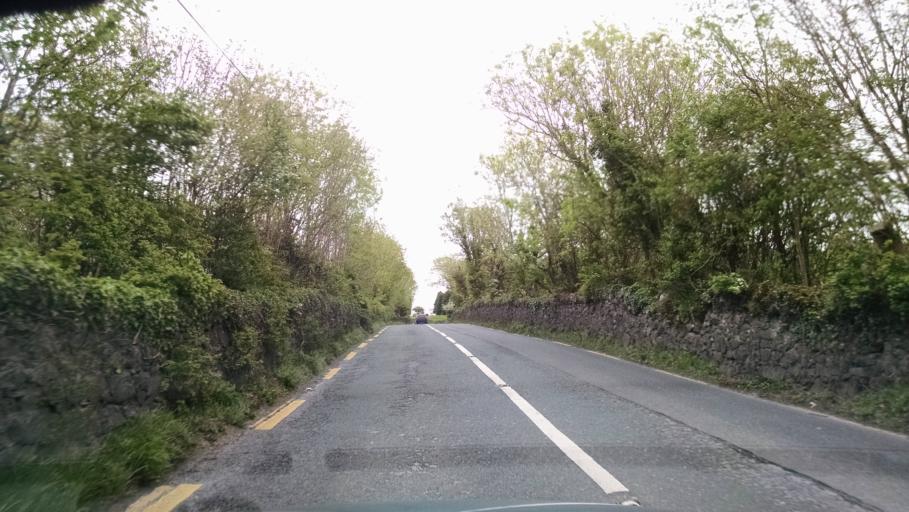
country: IE
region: Connaught
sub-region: County Galway
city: Moycullen
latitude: 53.4401
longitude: -9.0758
